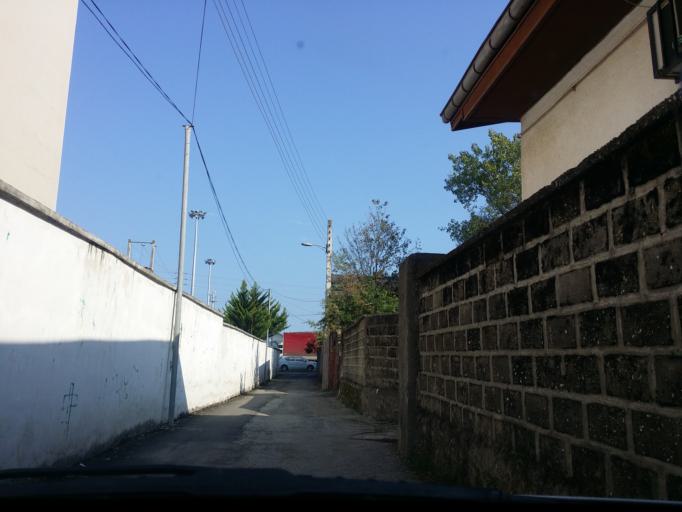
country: IR
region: Mazandaran
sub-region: Nowshahr
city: Nowshahr
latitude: 36.6505
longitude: 51.5112
